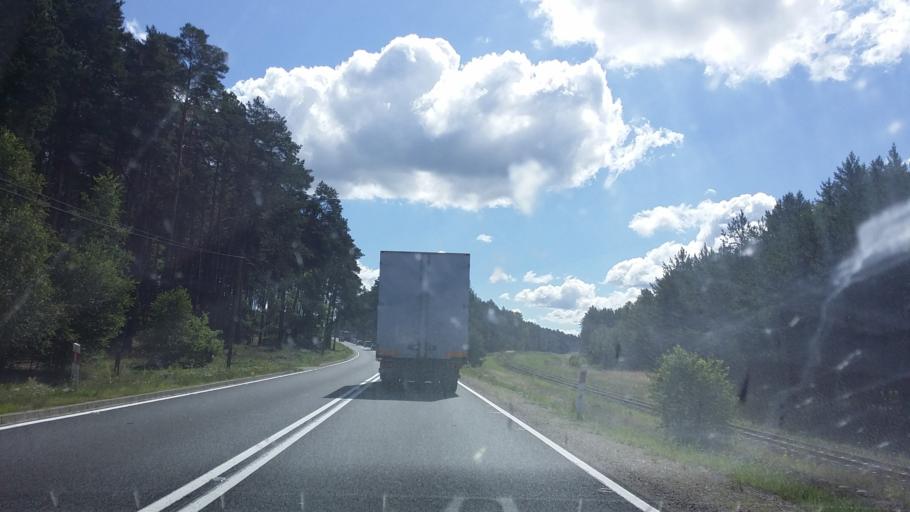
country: PL
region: West Pomeranian Voivodeship
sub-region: Powiat choszczenski
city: Drawno
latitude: 53.3025
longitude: 15.7915
